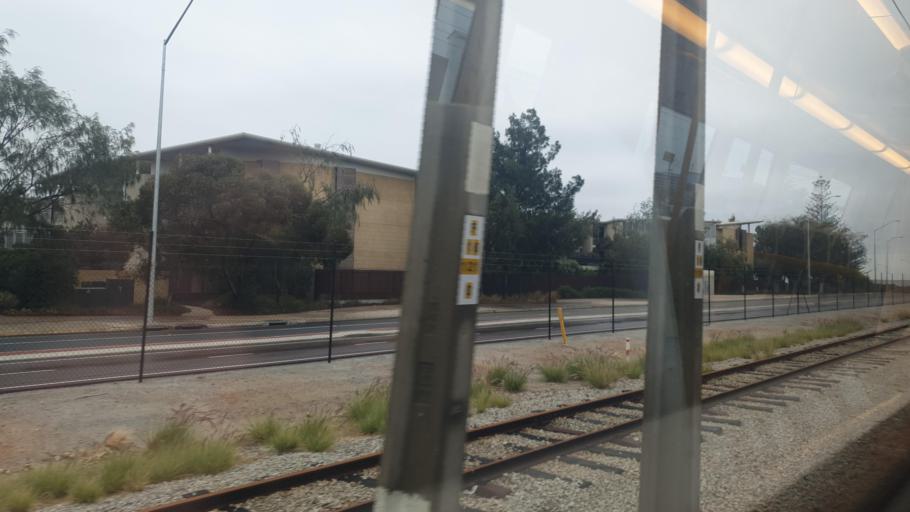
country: AU
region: Western Australia
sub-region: Fremantle
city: North Fremantle
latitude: -32.0286
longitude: 115.7518
